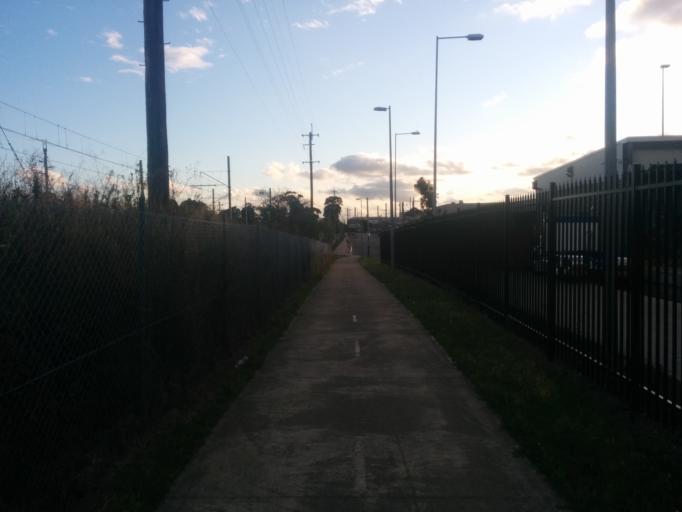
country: AU
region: New South Wales
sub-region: Fairfield
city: Fairfield East
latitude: -33.8627
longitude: 150.9740
